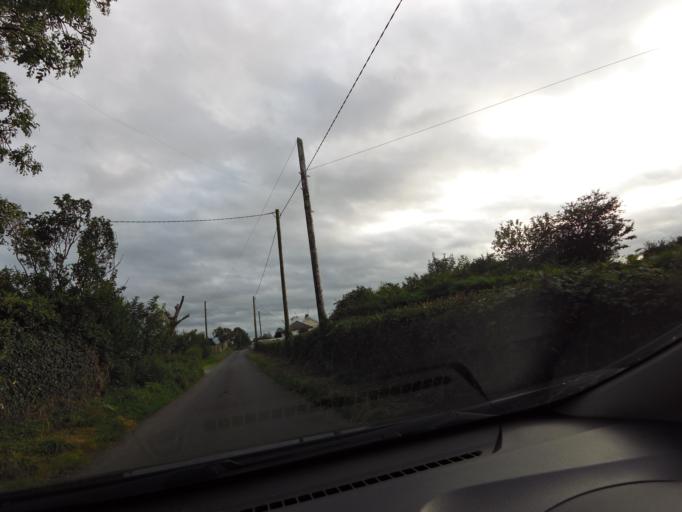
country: IE
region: Leinster
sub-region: Uibh Fhaili
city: Ferbane
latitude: 53.1813
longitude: -7.7266
